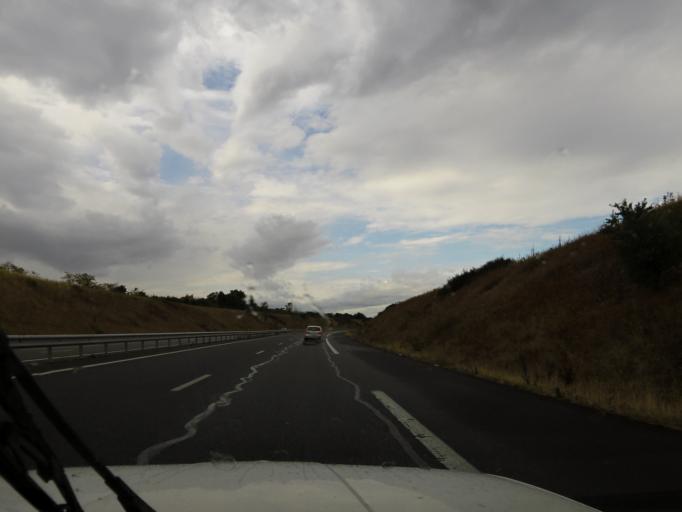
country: FR
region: Rhone-Alpes
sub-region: Departement de l'Isere
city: Satolas-et-Bonce
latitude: 45.7067
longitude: 5.0996
